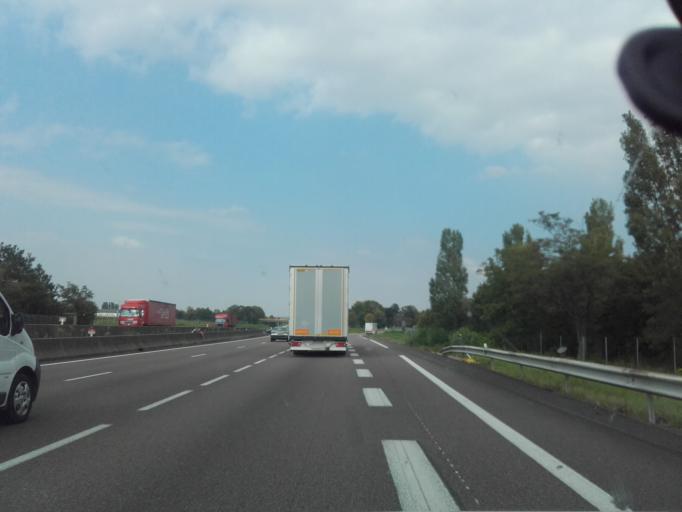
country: FR
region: Bourgogne
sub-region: Departement de Saone-et-Loire
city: Chatenoy-le-Royal
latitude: 46.8002
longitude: 4.8248
